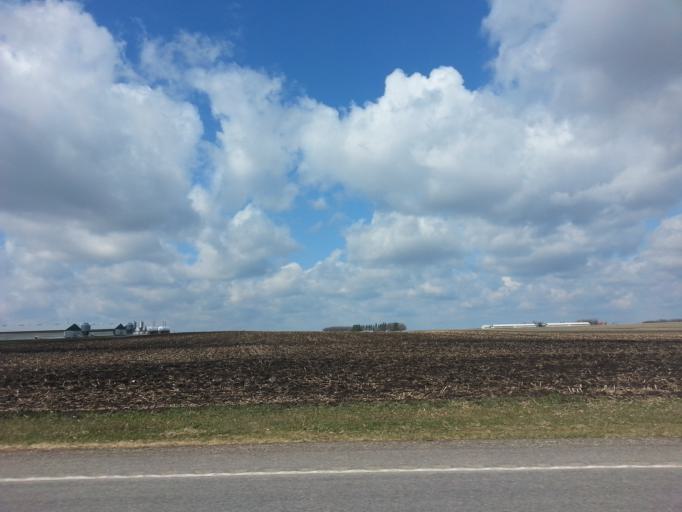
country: US
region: Minnesota
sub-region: Dodge County
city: Mantorville
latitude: 44.0800
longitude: -92.7366
